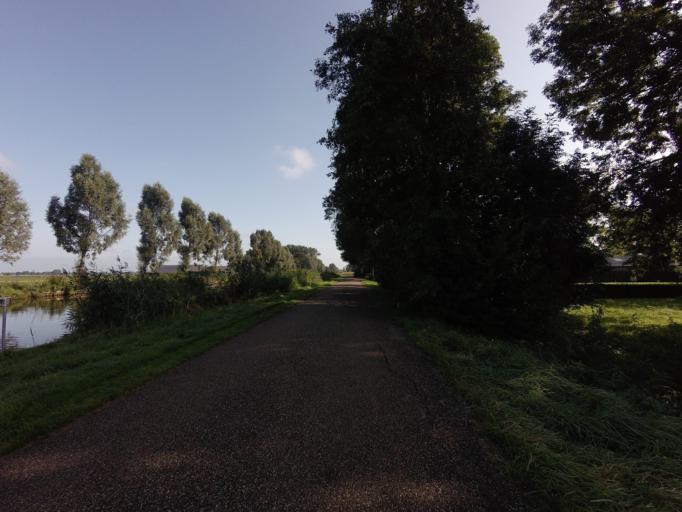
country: NL
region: Overijssel
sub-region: Gemeente Steenwijkerland
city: Steenwijkerwold
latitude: 52.7727
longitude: 6.0555
